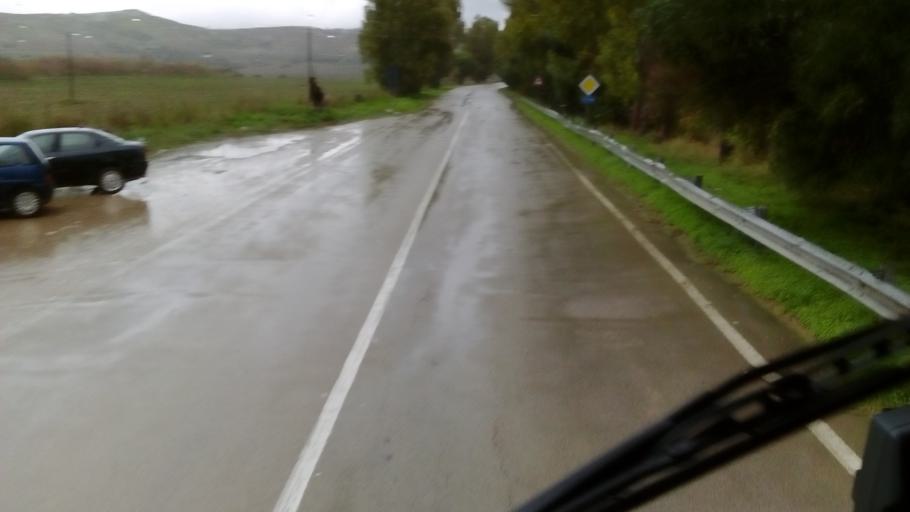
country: IT
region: Sicily
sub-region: Enna
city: Pietraperzia
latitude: 37.4927
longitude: 14.1505
